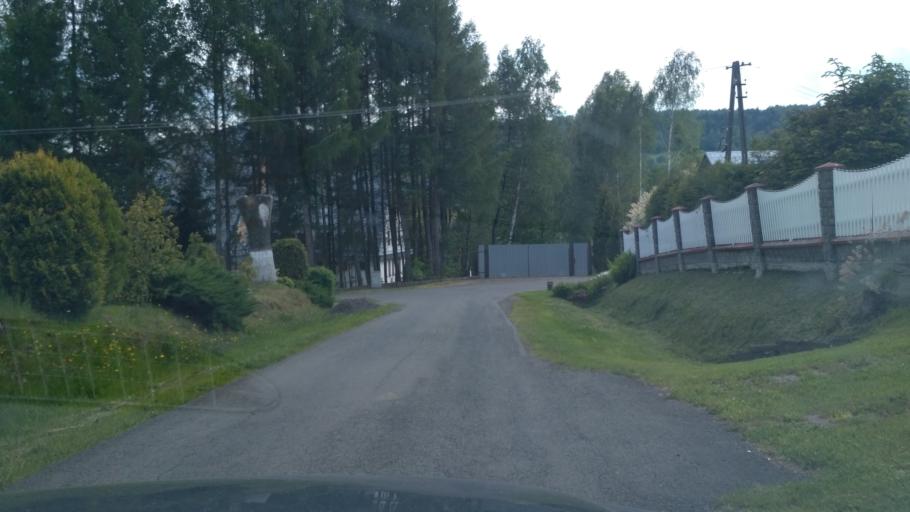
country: PL
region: Subcarpathian Voivodeship
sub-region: Powiat strzyzowski
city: Frysztak
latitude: 49.8747
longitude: 21.5815
